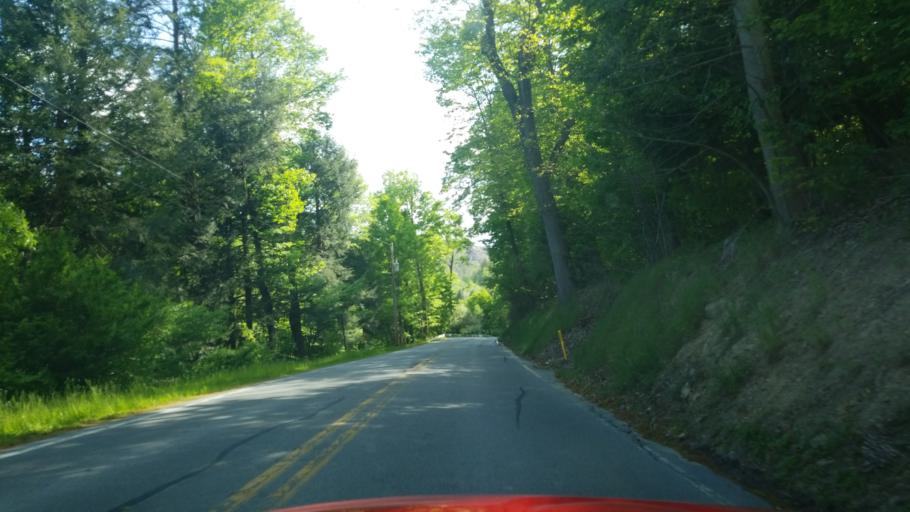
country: US
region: Pennsylvania
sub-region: Clearfield County
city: Hyde
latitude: 40.9753
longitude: -78.4800
